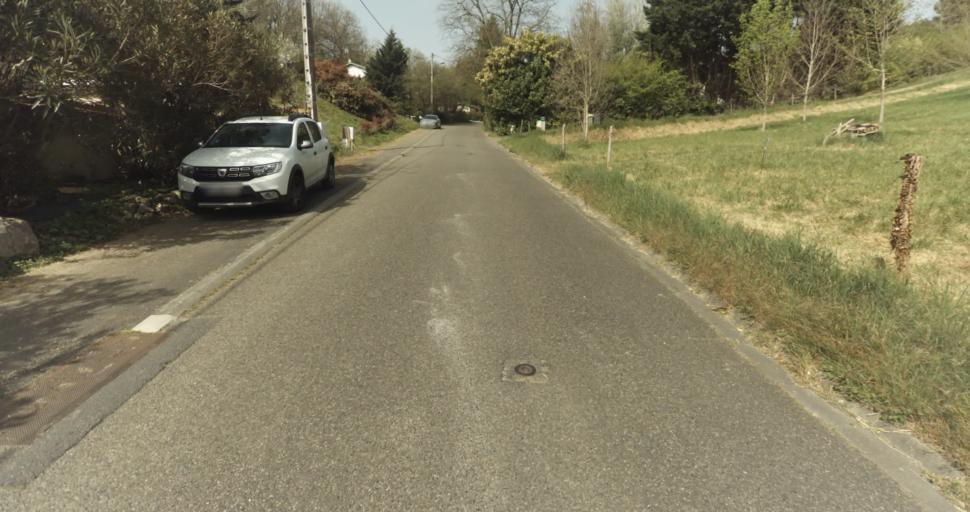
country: FR
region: Midi-Pyrenees
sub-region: Departement du Tarn-et-Garonne
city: Moissac
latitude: 44.1090
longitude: 1.0889
